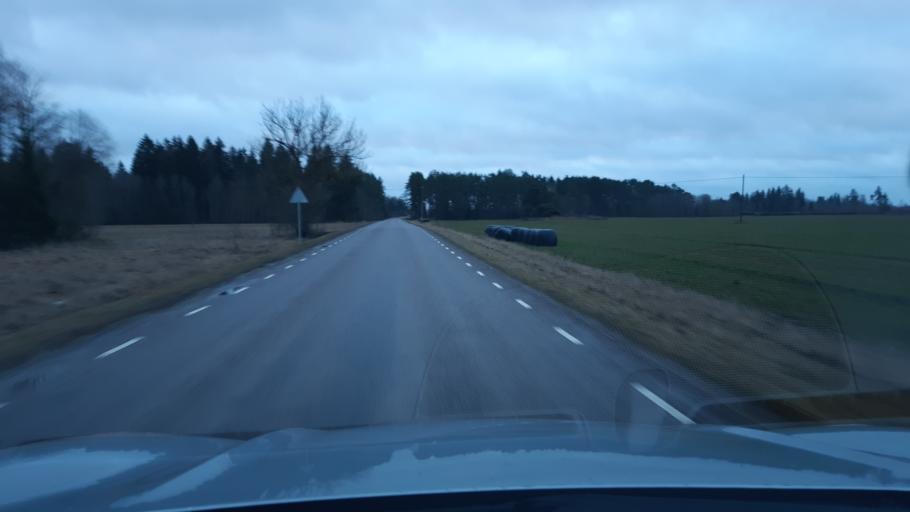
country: EE
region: Raplamaa
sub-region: Kohila vald
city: Kohila
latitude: 59.0768
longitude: 24.6792
